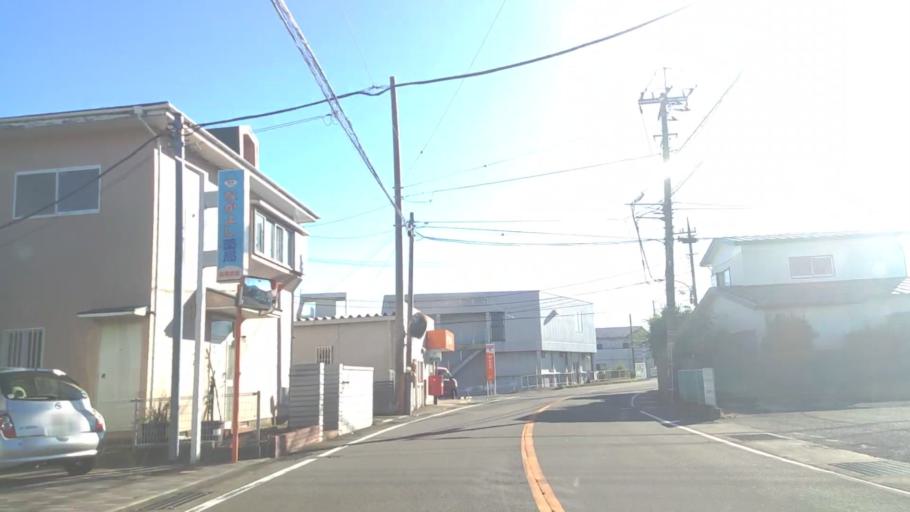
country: JP
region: Kanagawa
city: Atsugi
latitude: 35.4134
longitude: 139.3654
